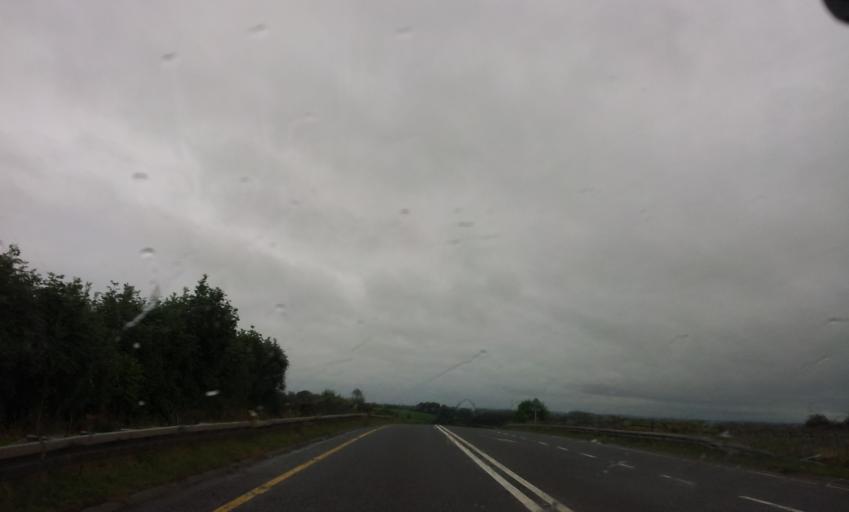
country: IE
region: Munster
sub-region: County Cork
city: Mitchelstown
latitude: 52.2740
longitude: -8.2824
